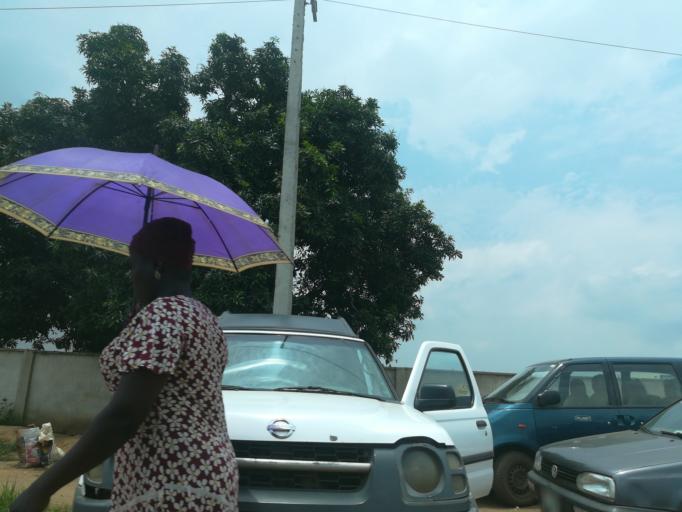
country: NG
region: Lagos
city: Ikorodu
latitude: 6.6166
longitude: 3.5663
